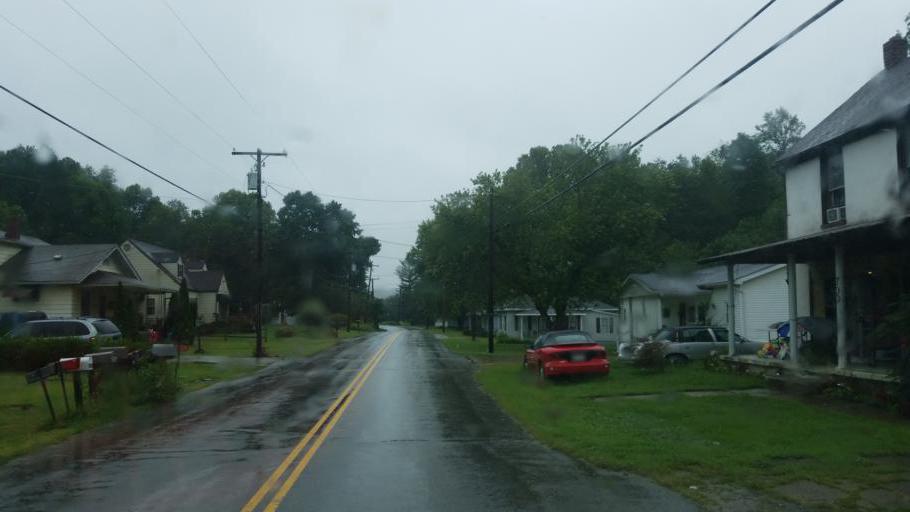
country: US
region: Ohio
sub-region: Scioto County
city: West Portsmouth
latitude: 38.7298
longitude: -83.0554
